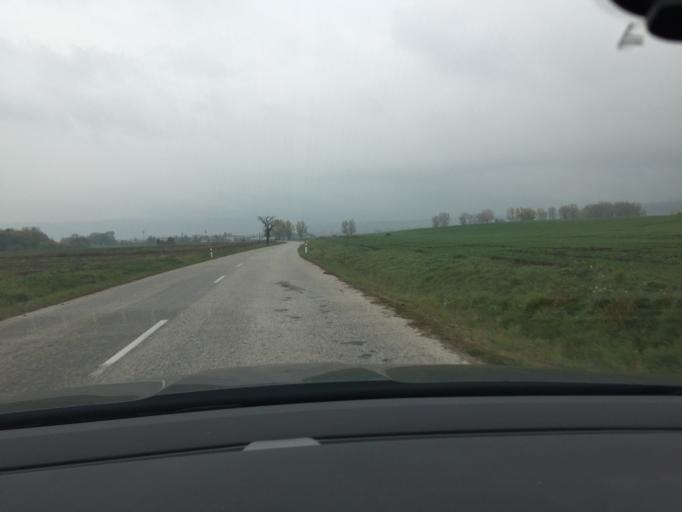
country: HU
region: Komarom-Esztergom
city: Esztergom
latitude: 47.9031
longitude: 18.7548
